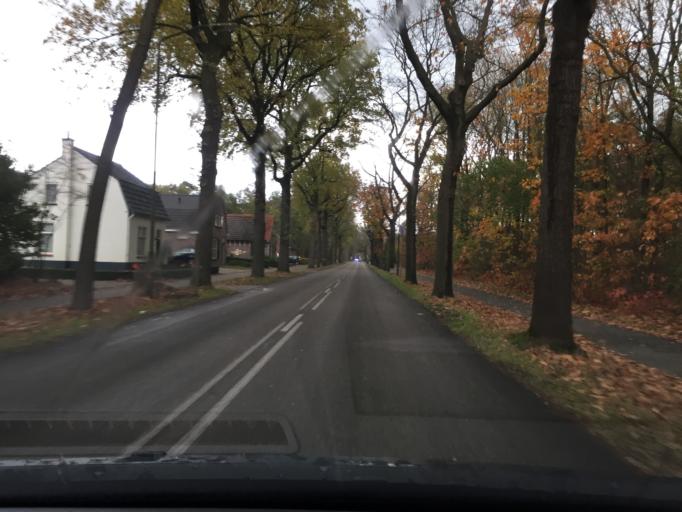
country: NL
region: North Brabant
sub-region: Gemeente Boekel
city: Boekel
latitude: 51.5716
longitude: 5.7080
